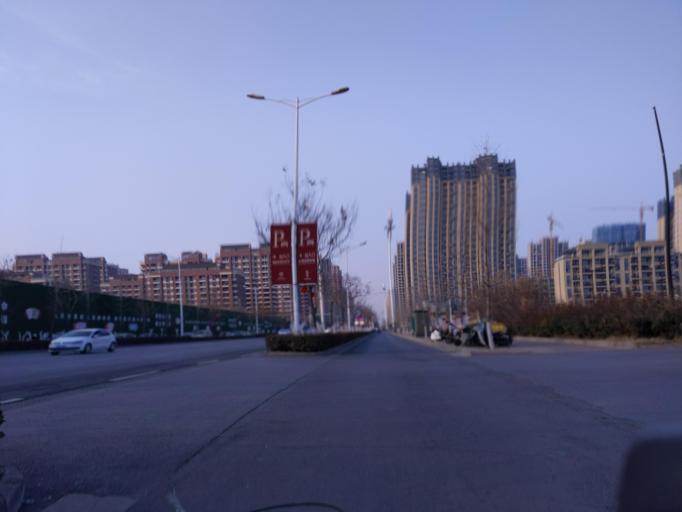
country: CN
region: Henan Sheng
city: Puyang
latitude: 35.7848
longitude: 115.0152
